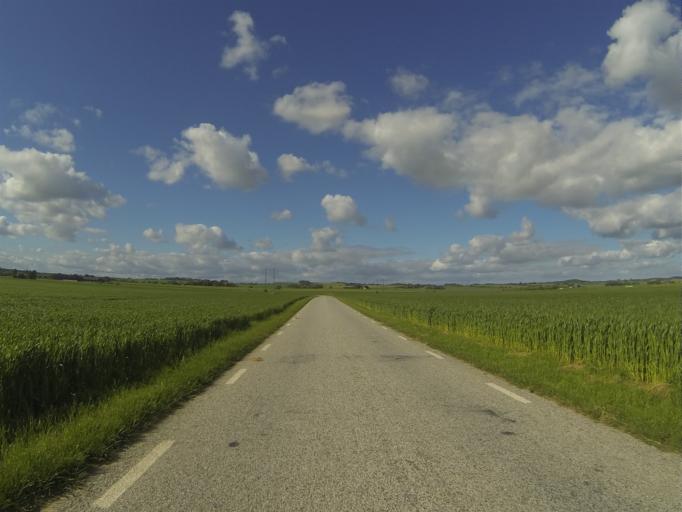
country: SE
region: Skane
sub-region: Staffanstorps Kommun
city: Staffanstorp
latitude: 55.6687
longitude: 13.2649
